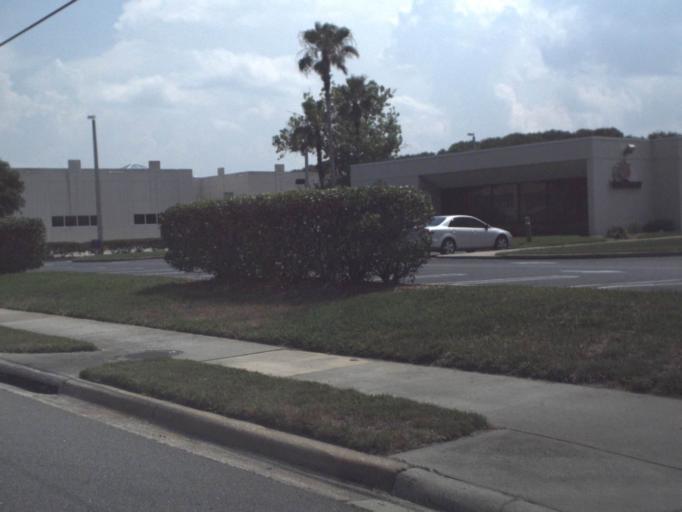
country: US
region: Florida
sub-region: Duval County
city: Neptune Beach
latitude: 30.3208
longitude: -81.3978
